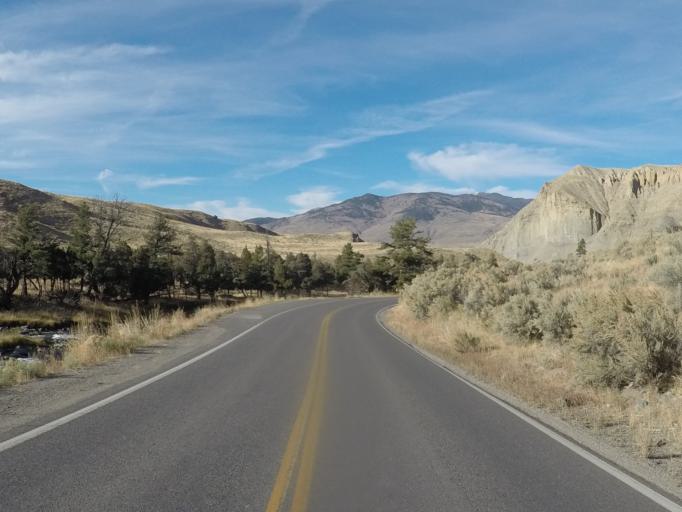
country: US
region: Montana
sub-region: Gallatin County
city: West Yellowstone
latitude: 45.0010
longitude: -110.6928
